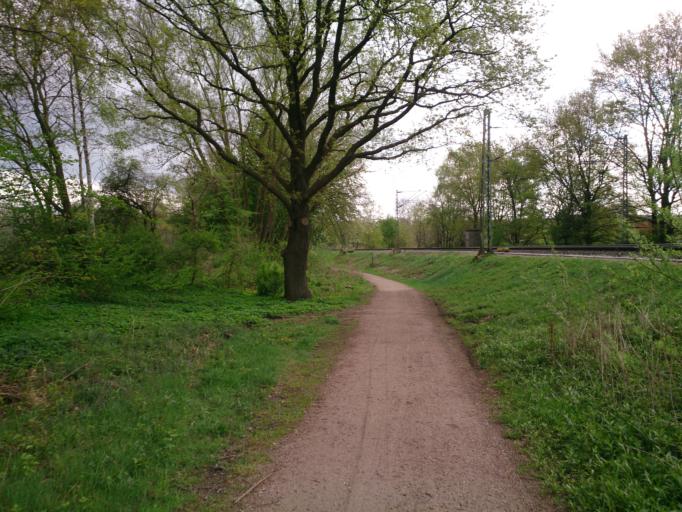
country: DE
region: Hamburg
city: Harburg
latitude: 53.4722
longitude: 9.9134
